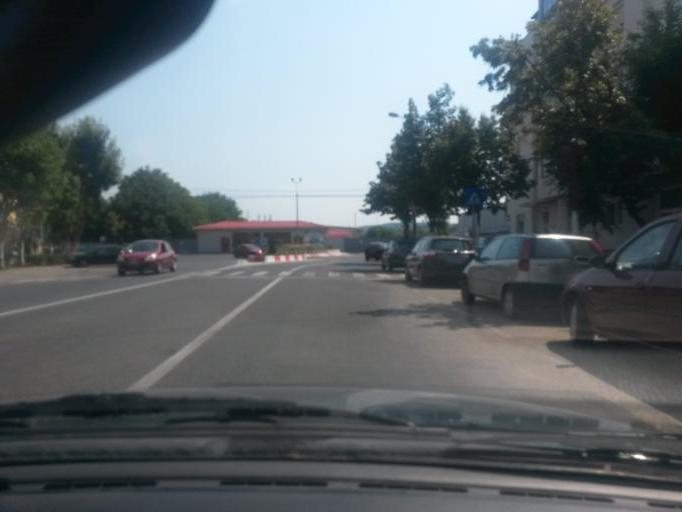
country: RO
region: Mures
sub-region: Comuna Corunca
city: Corunca
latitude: 46.5361
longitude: 24.5948
